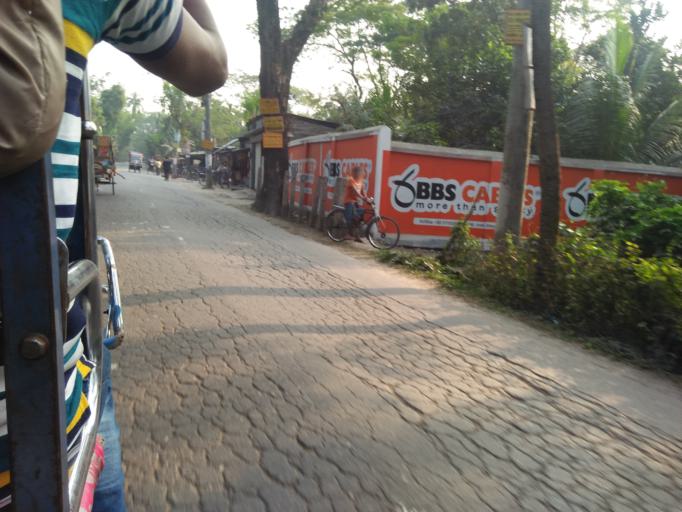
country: BD
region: Barisal
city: Bhola
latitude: 22.6982
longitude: 90.6430
